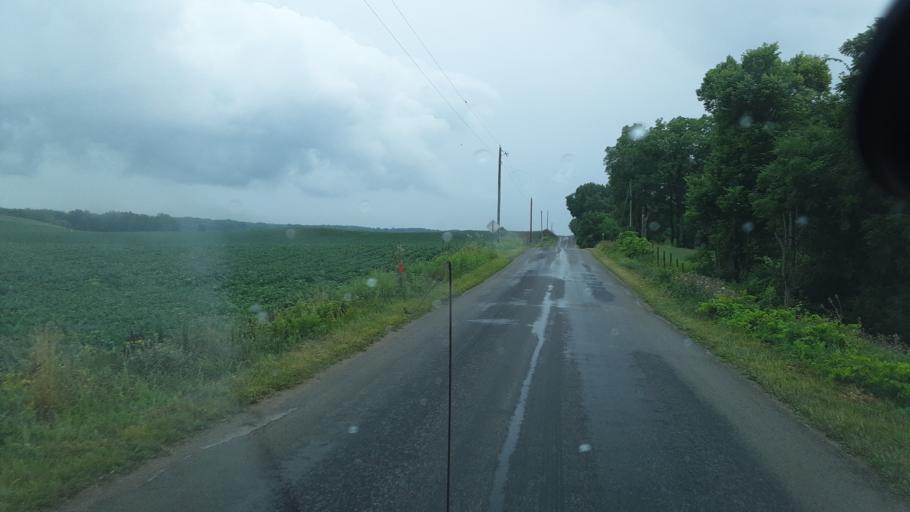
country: US
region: Indiana
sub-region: Steuben County
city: Hamilton
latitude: 41.5570
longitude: -84.8553
